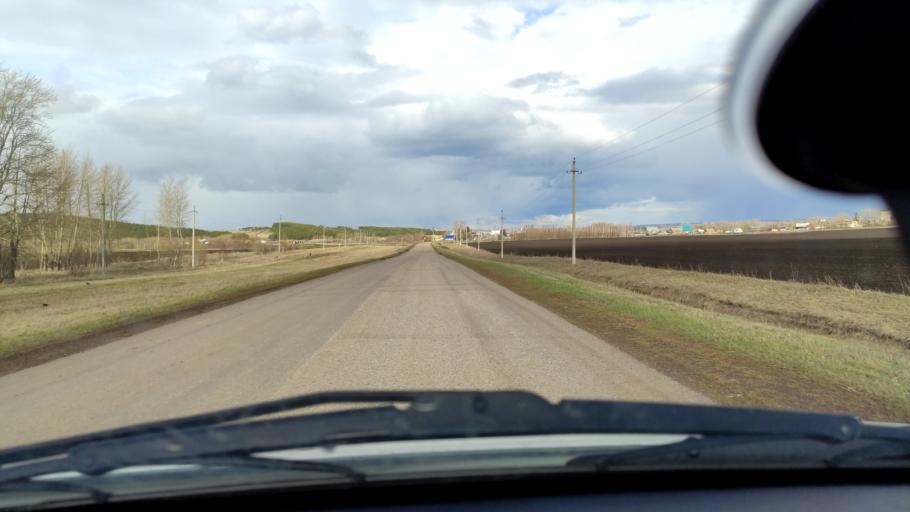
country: RU
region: Bashkortostan
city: Buzdyak
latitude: 54.7658
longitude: 54.5905
